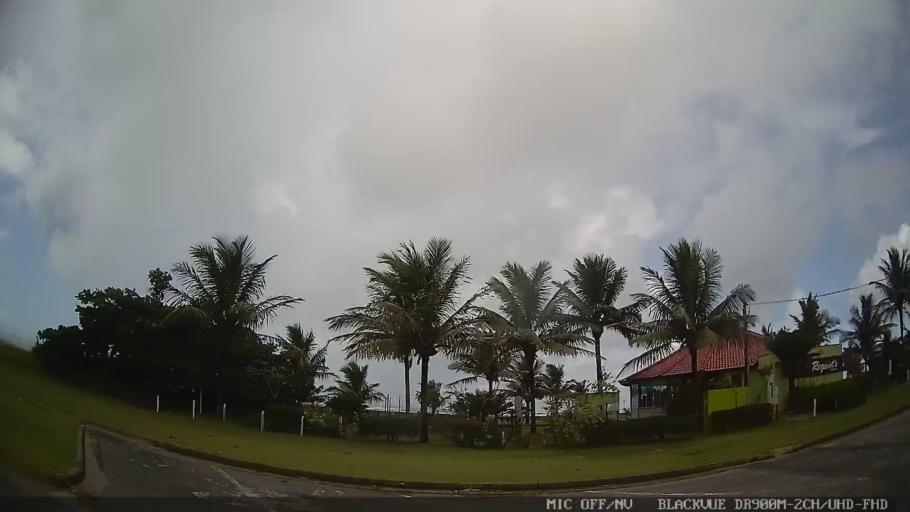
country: BR
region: Sao Paulo
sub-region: Itanhaem
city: Itanhaem
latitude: -24.2246
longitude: -46.8573
